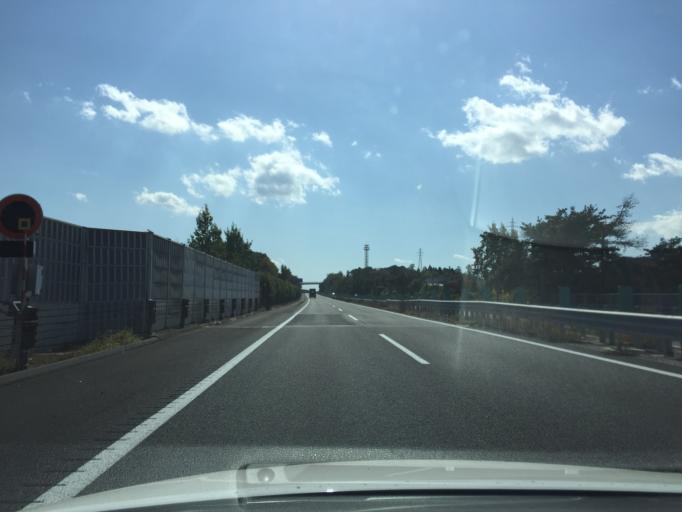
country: JP
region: Fukushima
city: Sukagawa
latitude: 37.2848
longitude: 140.3508
